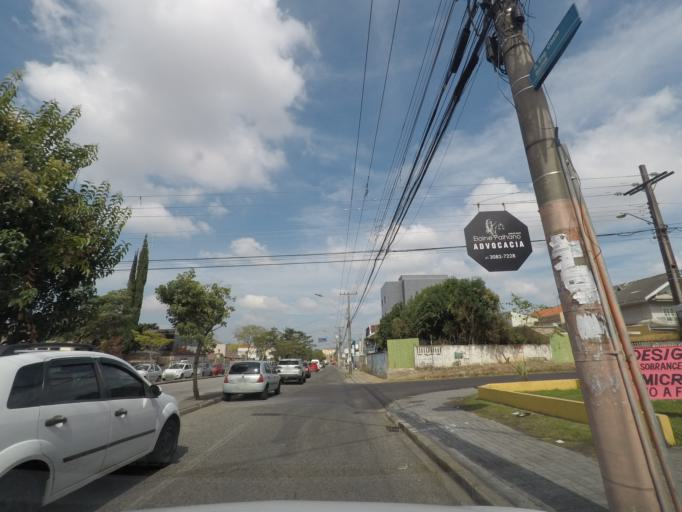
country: BR
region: Parana
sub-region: Pinhais
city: Pinhais
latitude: -25.4619
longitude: -49.2113
